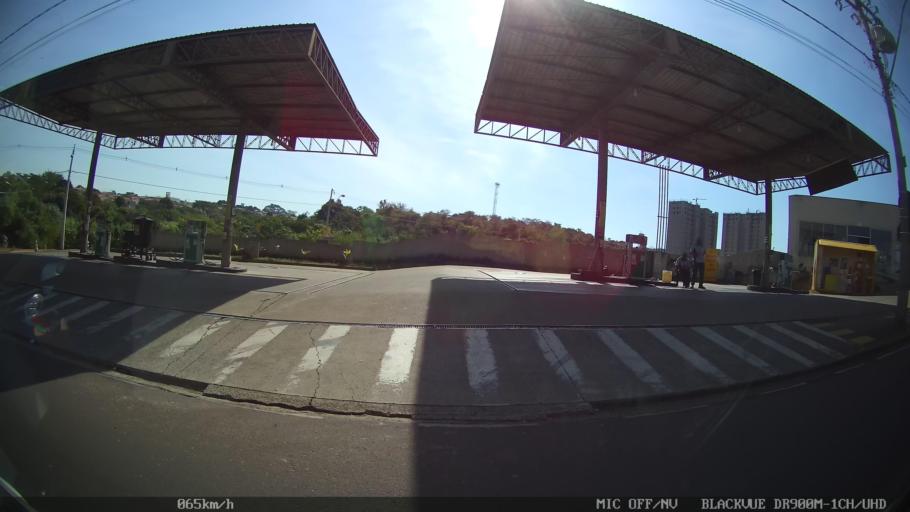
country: BR
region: Sao Paulo
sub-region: Sao Jose Do Rio Preto
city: Sao Jose do Rio Preto
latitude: -20.7925
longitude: -49.4237
